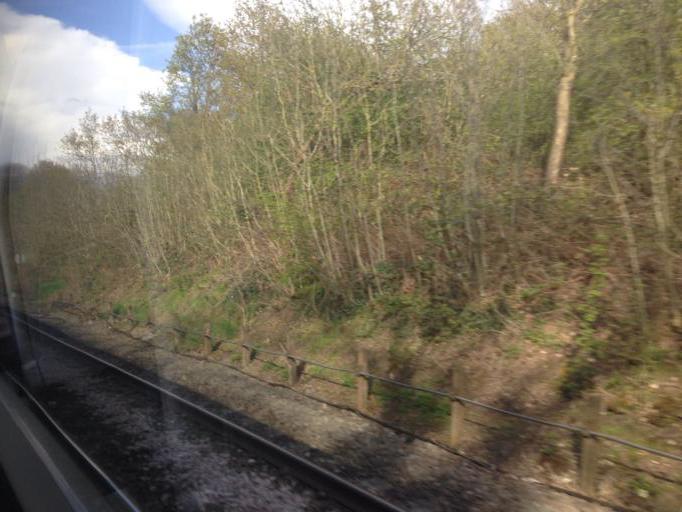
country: GB
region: England
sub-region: Greater London
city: Mitcham
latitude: 51.3977
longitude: -0.1603
